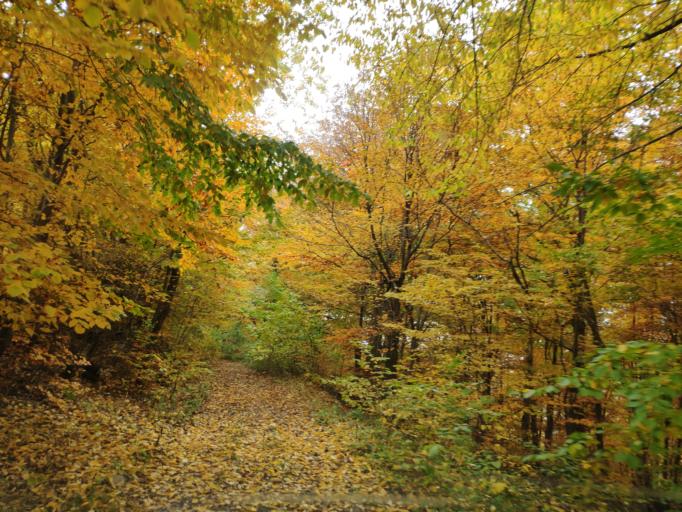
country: SK
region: Kosicky
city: Moldava nad Bodvou
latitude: 48.7233
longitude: 21.1013
